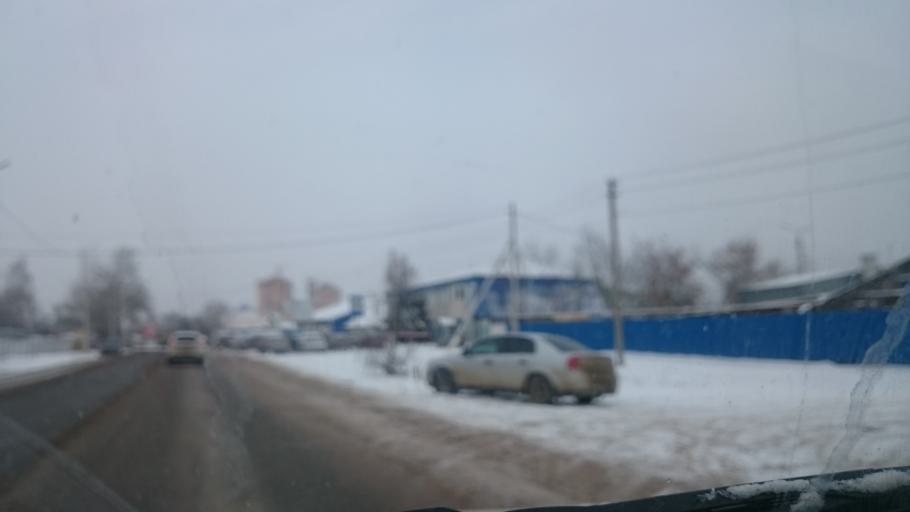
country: RU
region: Tula
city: Mendeleyevskiy
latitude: 54.1424
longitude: 37.5846
